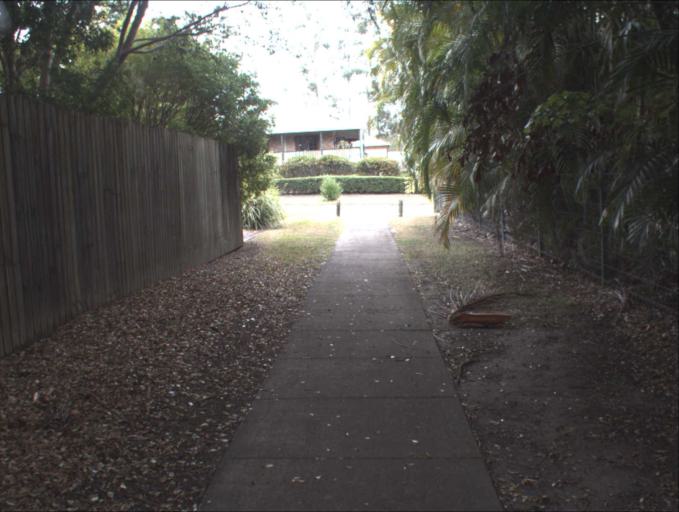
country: AU
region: Queensland
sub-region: Logan
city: Beenleigh
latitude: -27.6636
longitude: 153.2034
